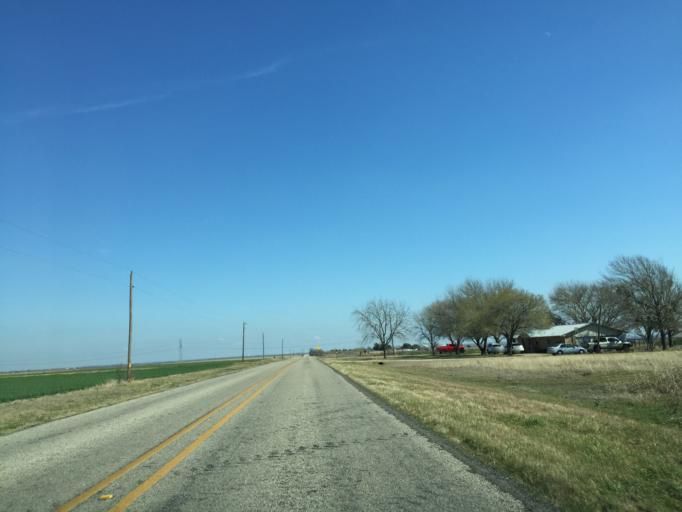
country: US
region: Texas
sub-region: Williamson County
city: Granger
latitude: 30.7569
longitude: -97.5344
